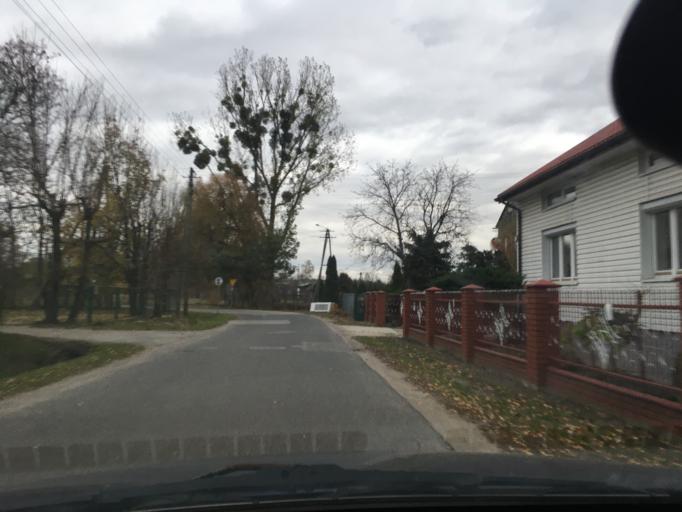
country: PL
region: Lodz Voivodeship
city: Zabia Wola
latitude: 52.0321
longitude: 20.6923
